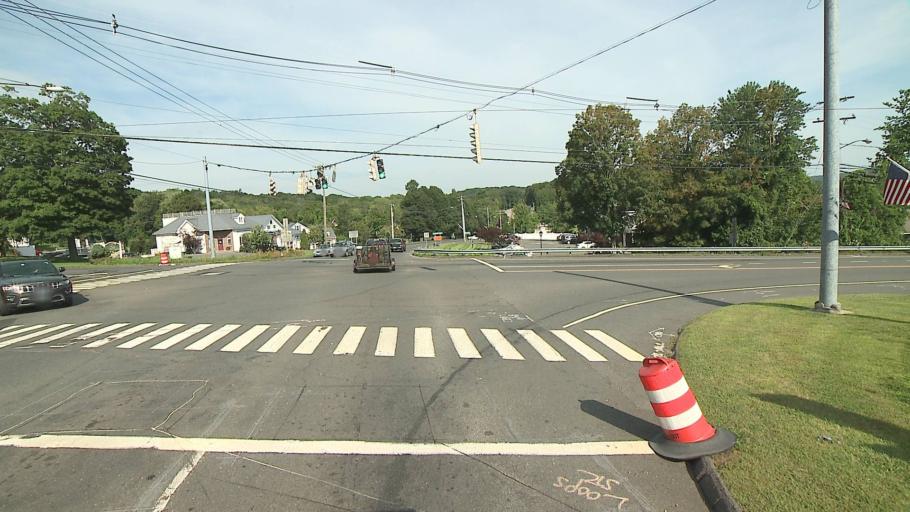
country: US
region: New York
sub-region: Putnam County
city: Putnam Lake
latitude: 41.4661
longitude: -73.4854
